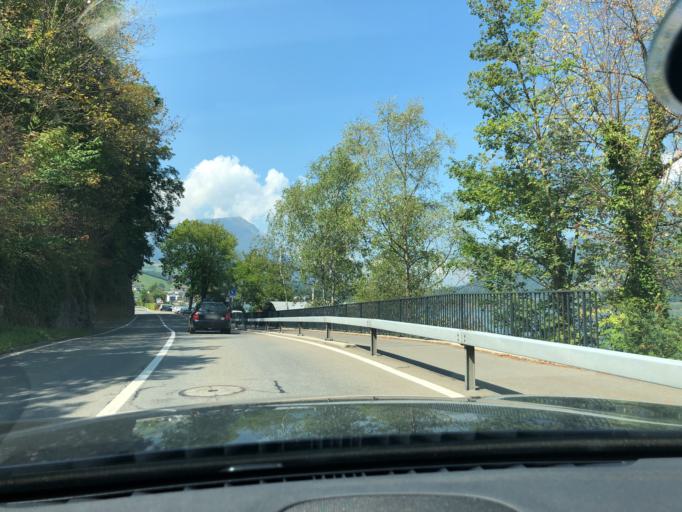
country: CH
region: Schwyz
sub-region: Bezirk Schwyz
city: Steinen
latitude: 47.0308
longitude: 8.5970
